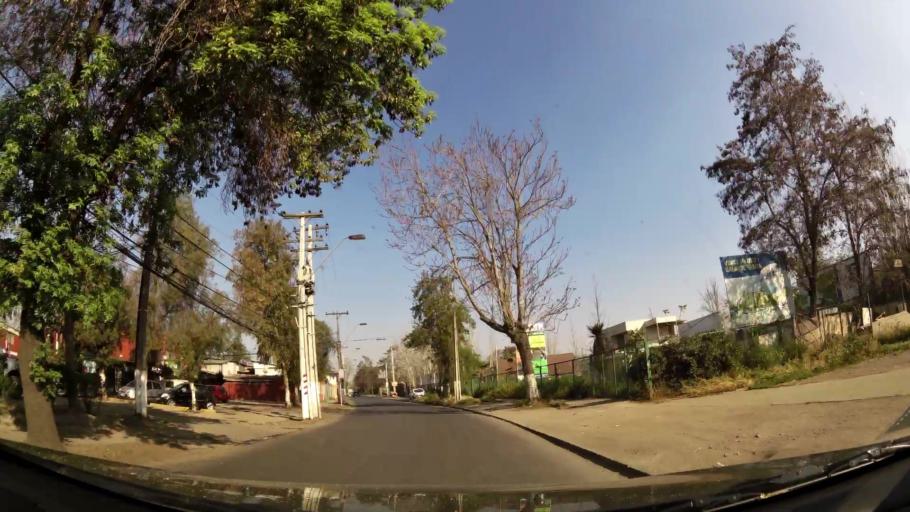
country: CL
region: Santiago Metropolitan
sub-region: Provincia de Santiago
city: Santiago
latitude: -33.3945
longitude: -70.6761
